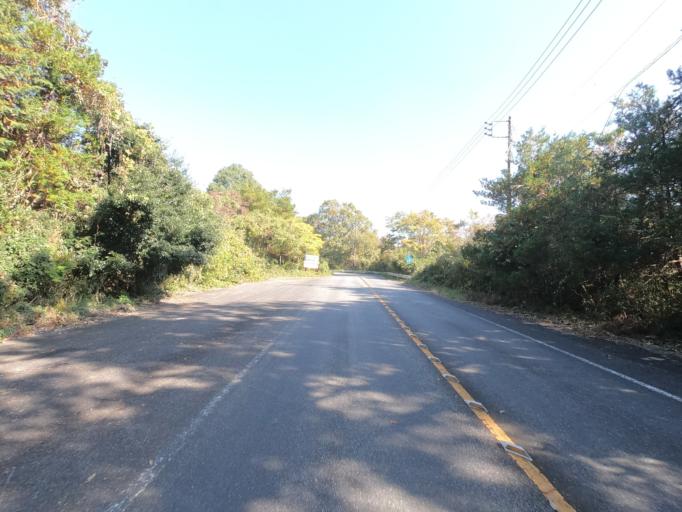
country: JP
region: Ibaraki
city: Tsukuba
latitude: 36.1632
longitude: 140.1750
